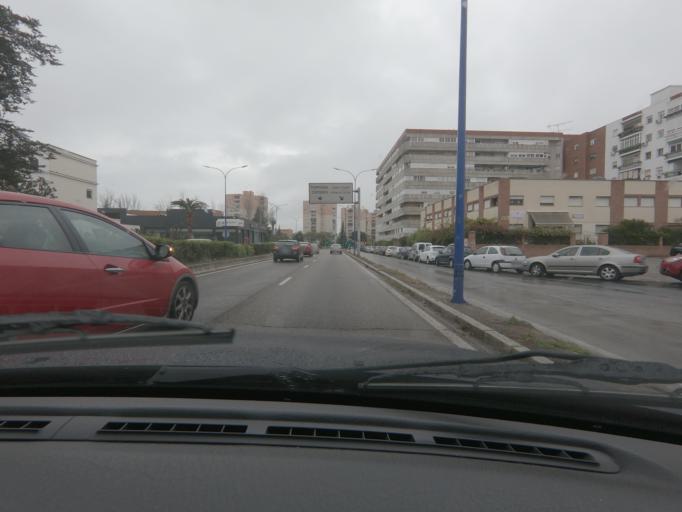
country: ES
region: Extremadura
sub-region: Provincia de Badajoz
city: Badajoz
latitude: 38.8718
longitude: -6.9797
